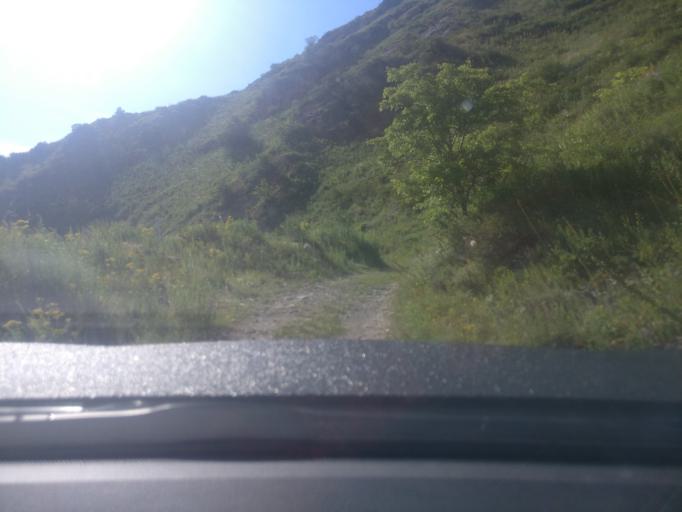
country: KZ
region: Almaty Qalasy
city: Almaty
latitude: 43.1067
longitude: 76.9442
